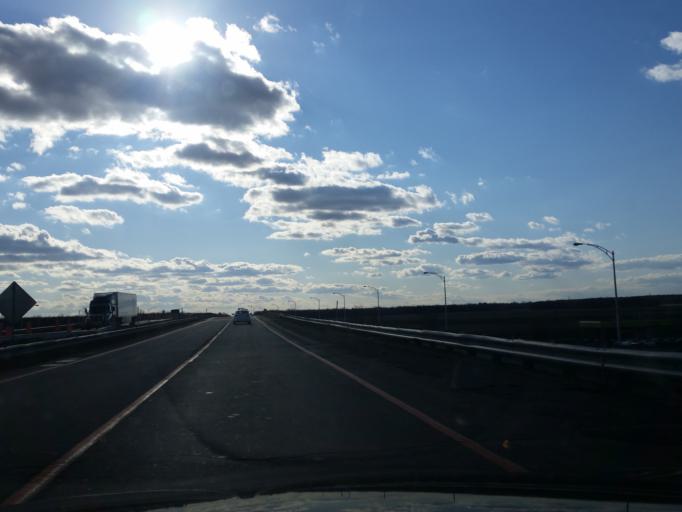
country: CA
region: Quebec
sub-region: Lanaudiere
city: Berthierville
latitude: 46.0891
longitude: -73.1977
